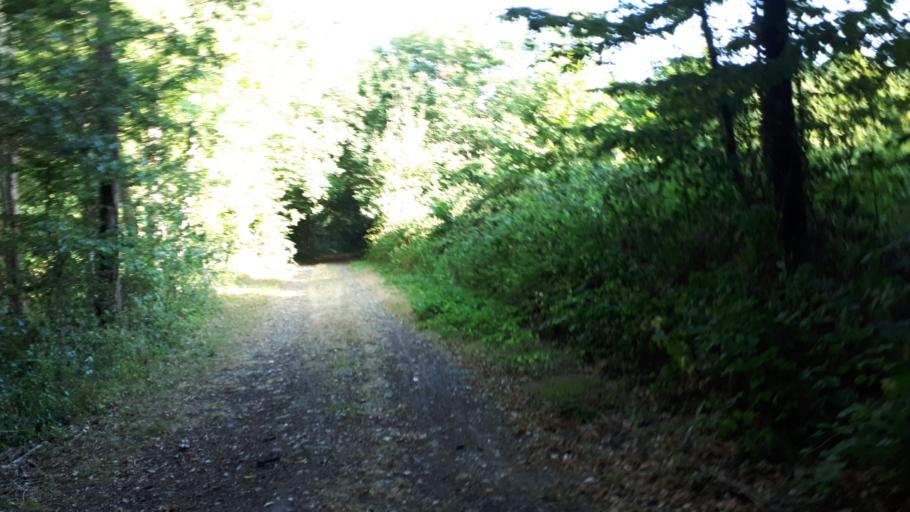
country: FR
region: Centre
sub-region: Departement du Loir-et-Cher
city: Villiers-sur-Loir
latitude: 47.7913
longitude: 0.9809
